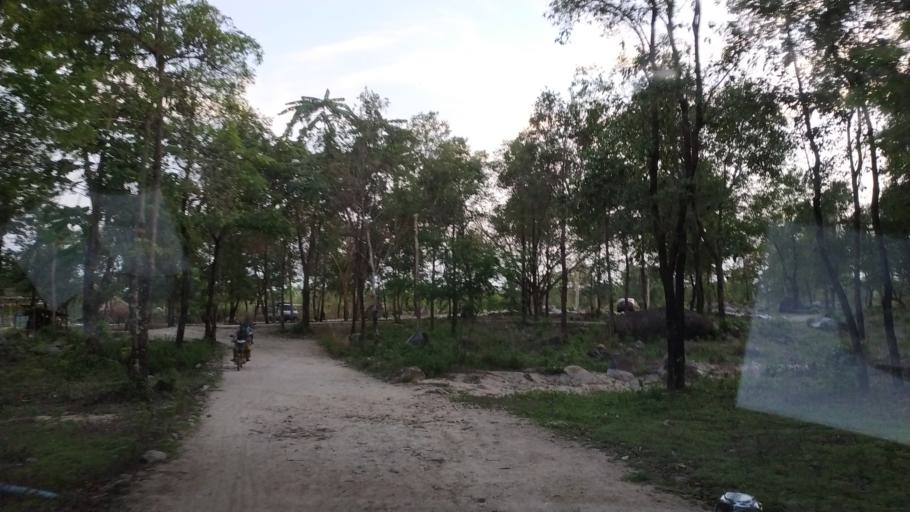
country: MM
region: Mon
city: Kyaikto
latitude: 17.4382
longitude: 97.0399
